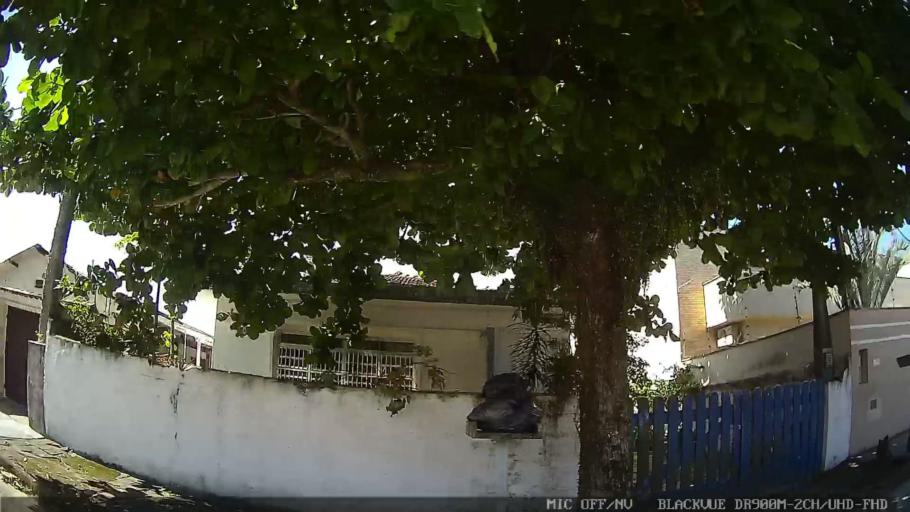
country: BR
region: Sao Paulo
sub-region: Peruibe
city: Peruibe
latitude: -24.3141
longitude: -46.9918
